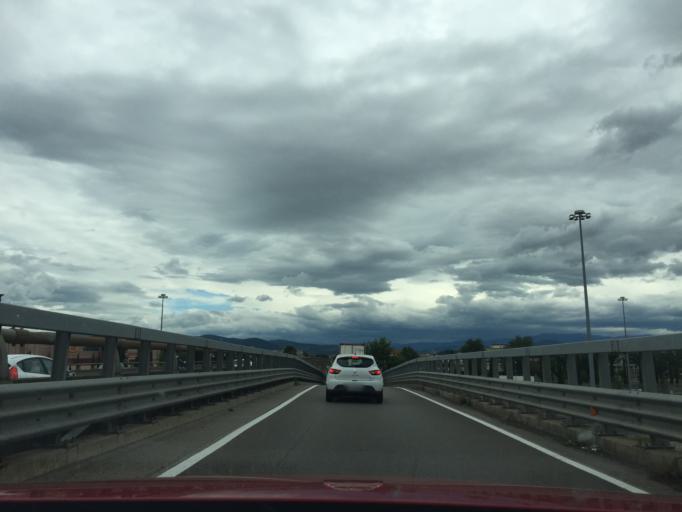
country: IT
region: Tuscany
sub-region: Province of Florence
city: Scandicci
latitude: 43.7704
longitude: 11.1852
